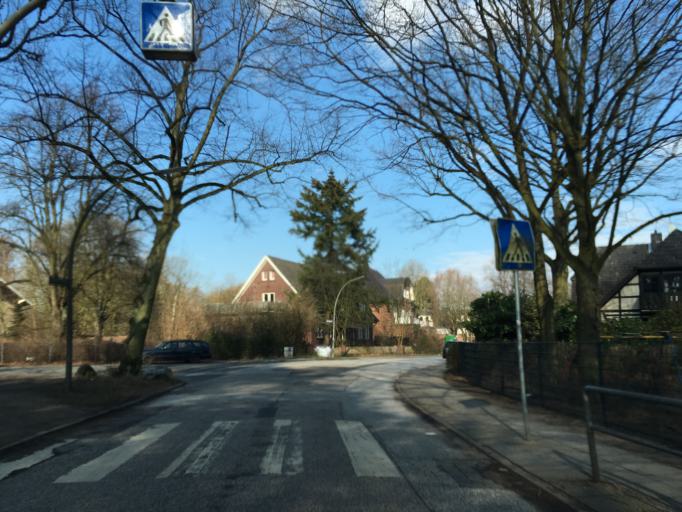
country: DE
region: Hamburg
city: Eidelstedt
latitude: 53.5670
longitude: 9.8780
